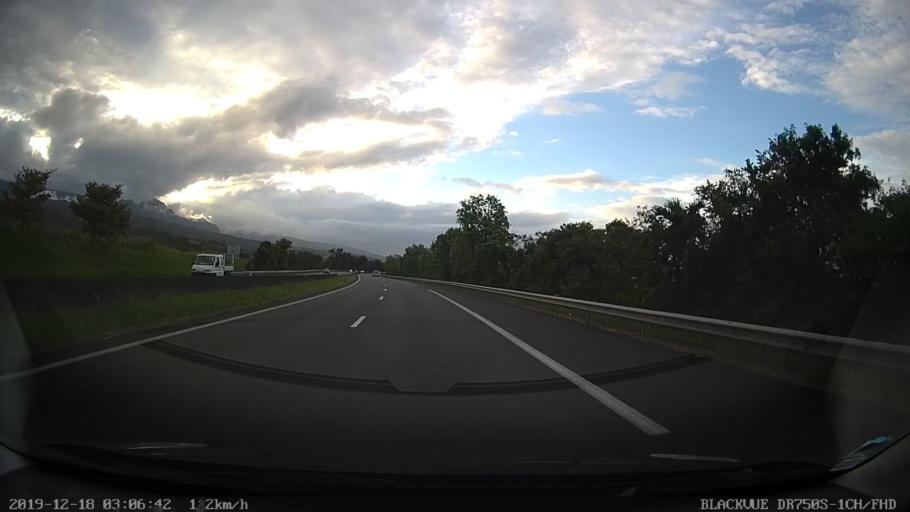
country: RE
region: Reunion
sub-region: Reunion
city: Bras-Panon
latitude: -21.0069
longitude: 55.6832
